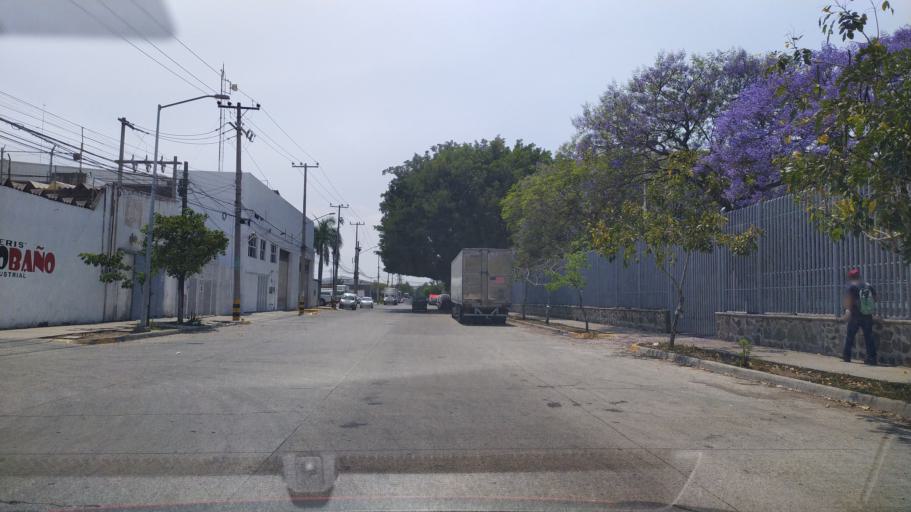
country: MX
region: Jalisco
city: Guadalajara
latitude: 20.6428
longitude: -103.3668
